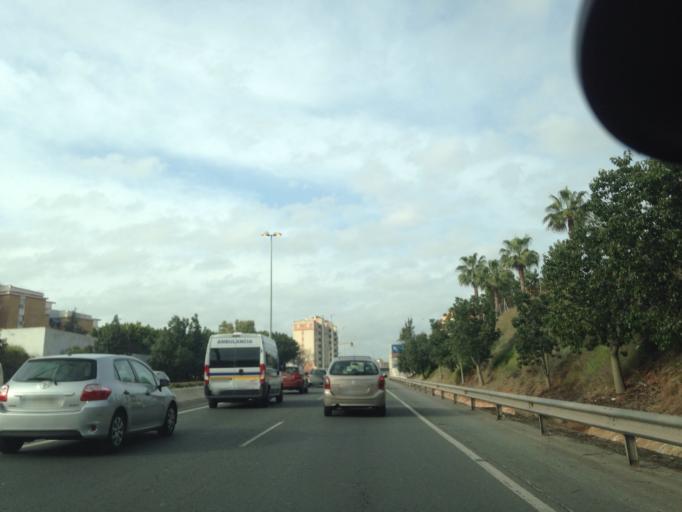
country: ES
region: Andalusia
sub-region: Provincia de Malaga
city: Malaga
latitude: 36.7271
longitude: -4.4493
